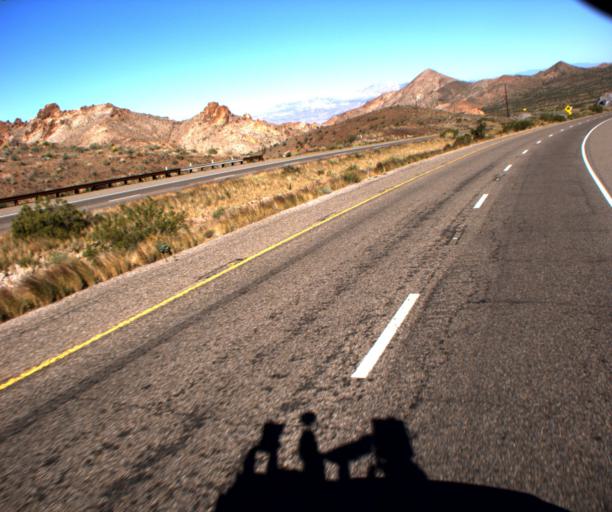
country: US
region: Arizona
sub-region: Mohave County
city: Bullhead City
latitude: 35.1948
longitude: -114.4116
